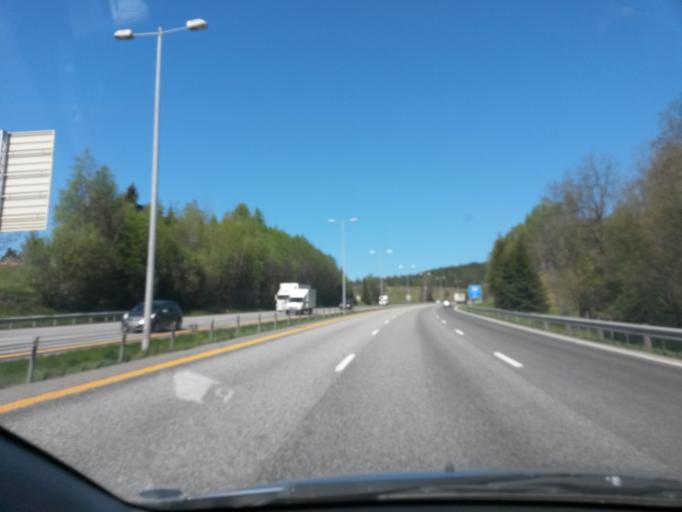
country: NO
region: Buskerud
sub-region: Lier
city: Tranby
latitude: 59.8005
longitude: 10.2686
